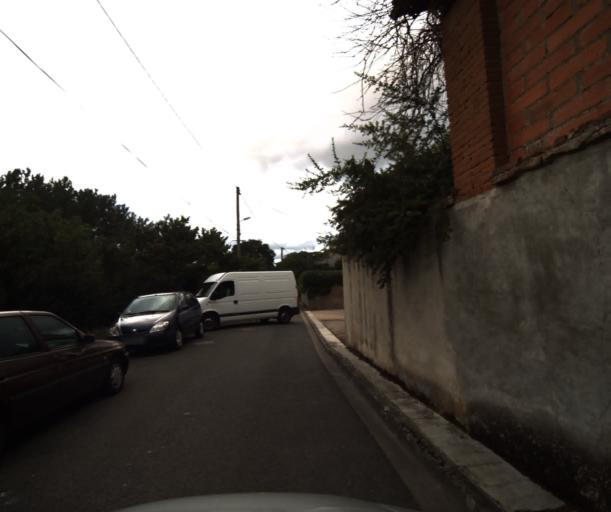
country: FR
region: Midi-Pyrenees
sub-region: Departement de la Haute-Garonne
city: Le Fauga
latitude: 43.4154
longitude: 1.3105
